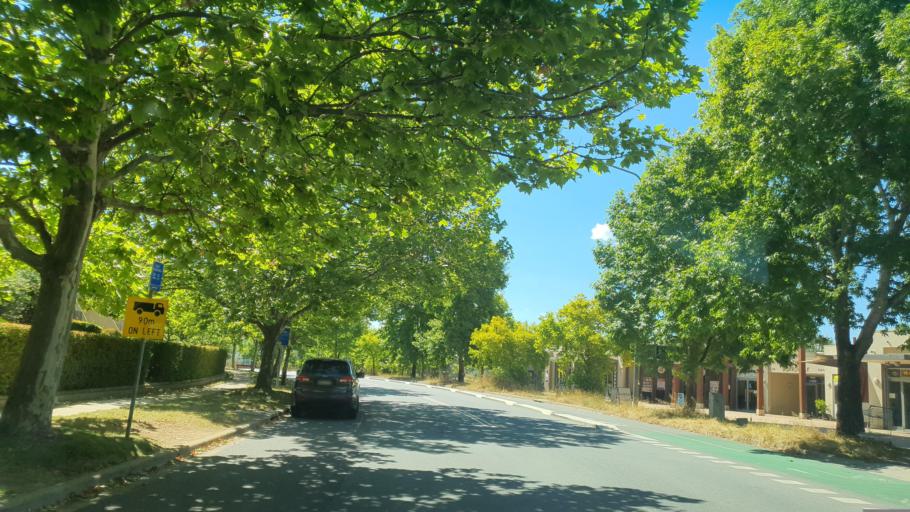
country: AU
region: Australian Capital Territory
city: Macquarie
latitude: -35.2365
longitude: 149.0700
